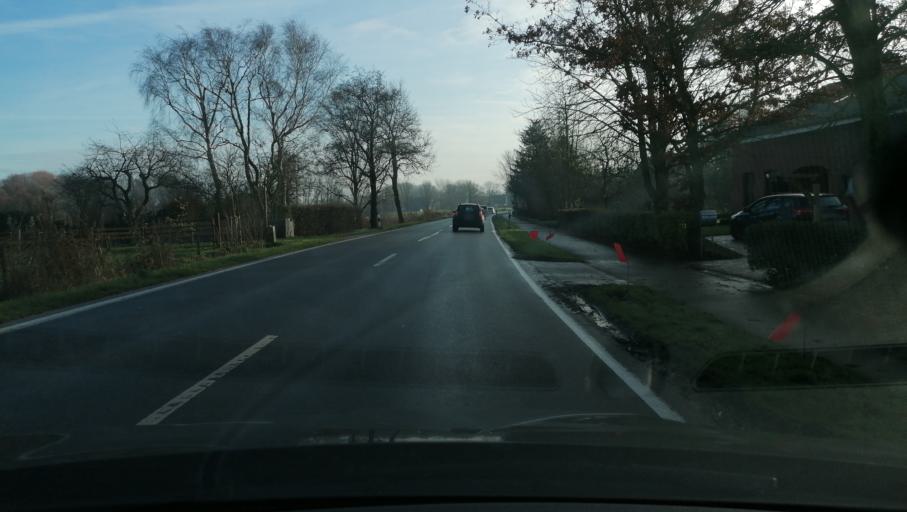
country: DE
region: Schleswig-Holstein
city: Epenwohrden
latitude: 54.1093
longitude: 9.0266
